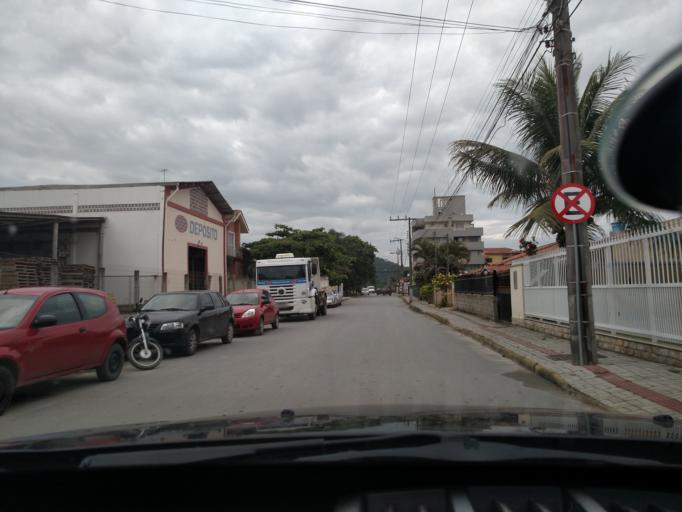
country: BR
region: Santa Catarina
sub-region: Porto Belo
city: Porto Belo
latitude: -27.1473
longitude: -48.5063
